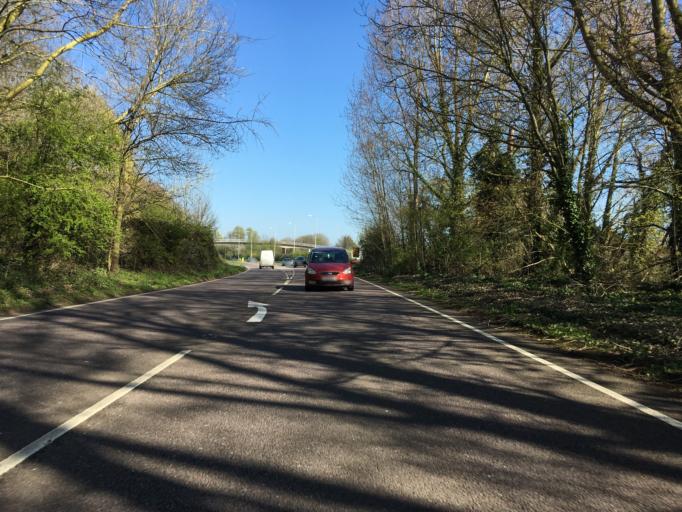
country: GB
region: England
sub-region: North Somerset
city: Easton-in-Gordano
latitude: 51.4764
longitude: -2.7296
